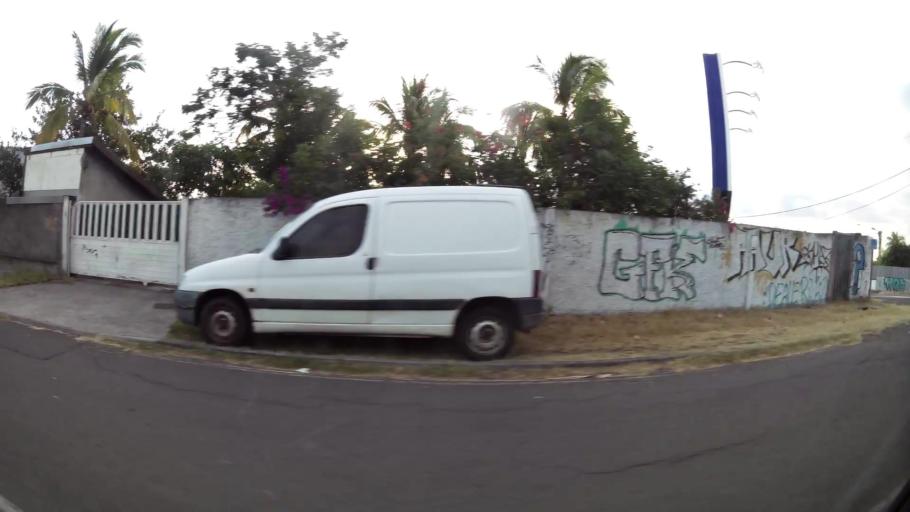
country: RE
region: Reunion
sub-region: Reunion
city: Saint-Paul
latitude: -21.0402
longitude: 55.2232
